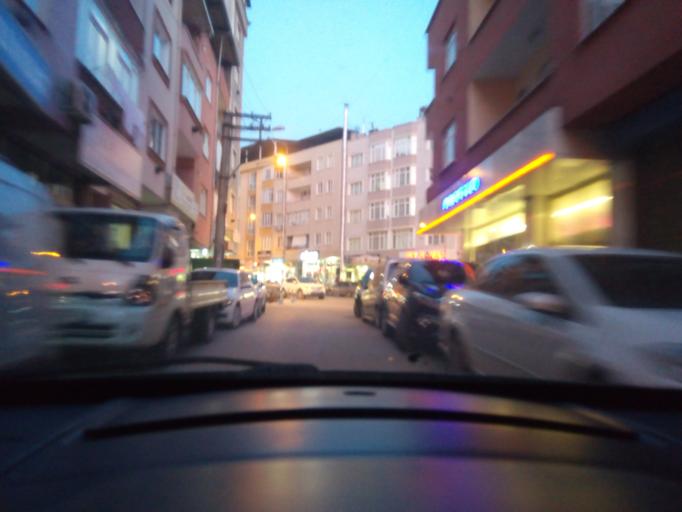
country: TR
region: Bursa
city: Niluefer
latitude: 40.2562
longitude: 28.9599
